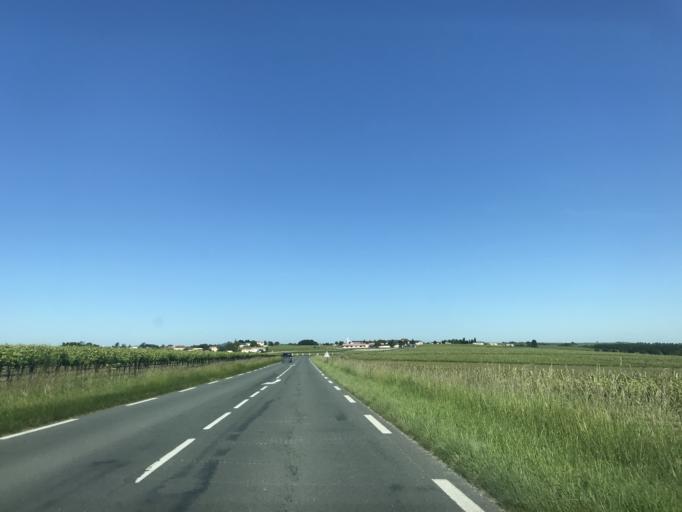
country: FR
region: Poitou-Charentes
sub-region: Departement de la Charente-Maritime
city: Perignac
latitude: 45.5528
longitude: -0.3687
